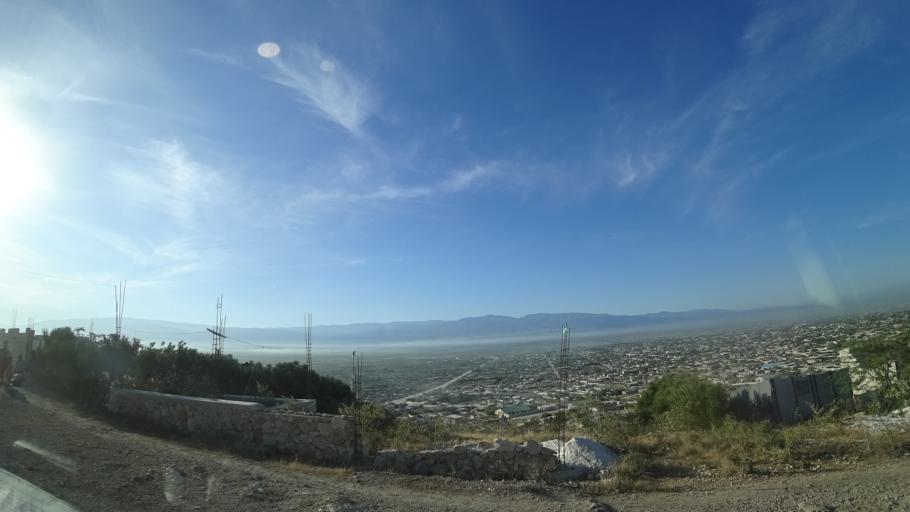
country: HT
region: Ouest
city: Croix des Bouquets
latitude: 18.6696
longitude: -72.2263
